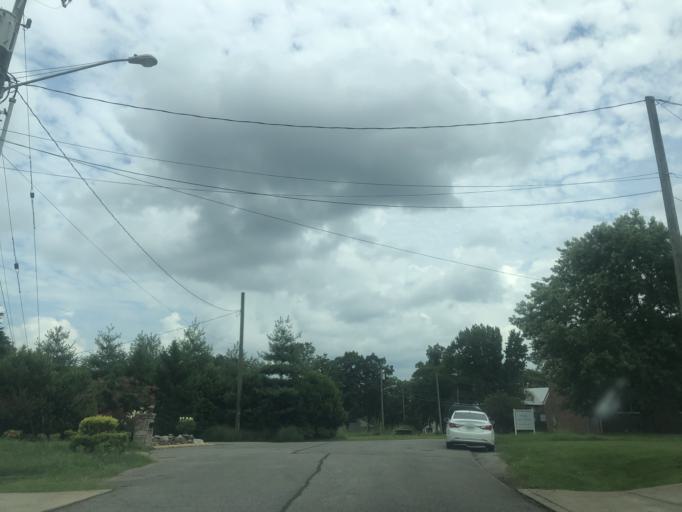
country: US
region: Tennessee
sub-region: Davidson County
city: Oak Hill
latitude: 36.0968
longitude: -86.7980
